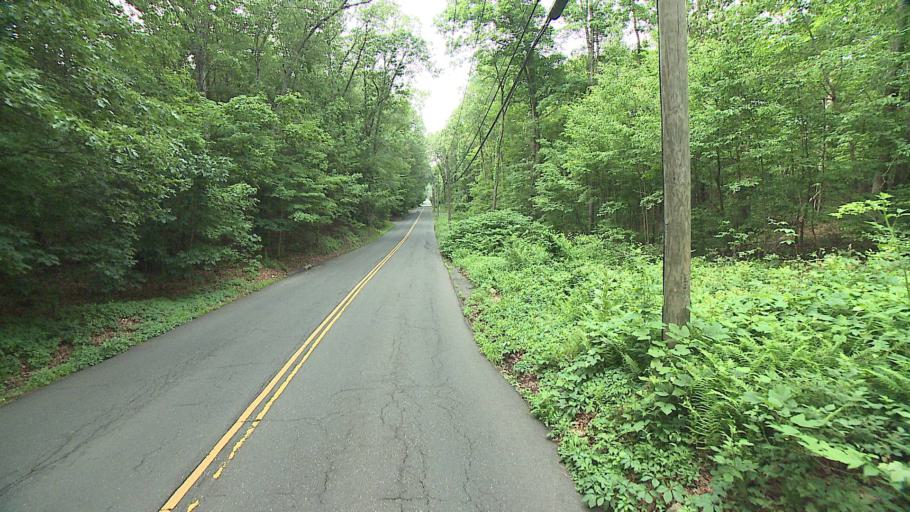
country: US
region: Connecticut
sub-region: New Haven County
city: Southbury
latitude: 41.4616
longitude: -73.1993
